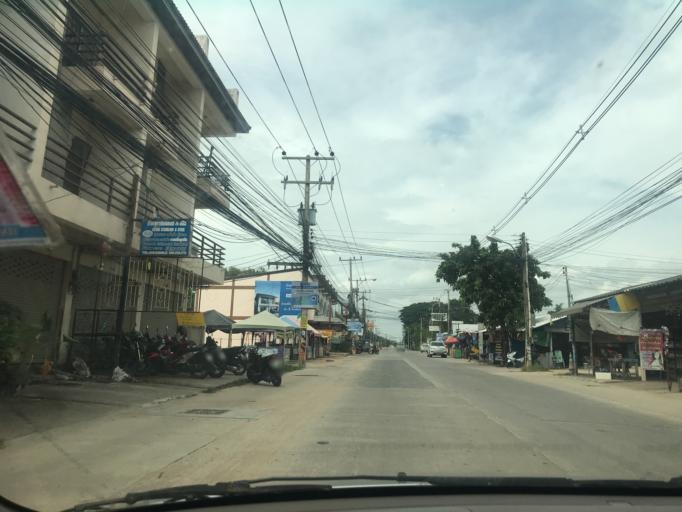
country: TH
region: Chon Buri
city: Phatthaya
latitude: 12.8835
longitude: 100.9125
